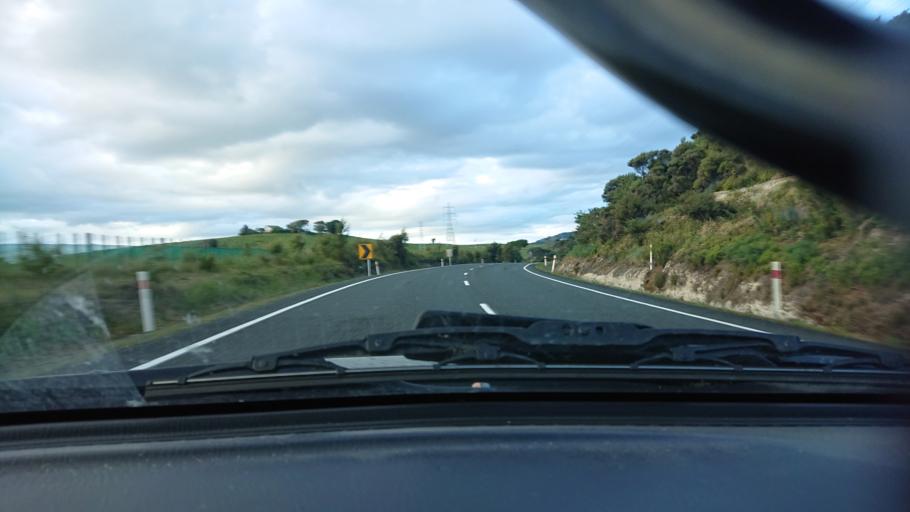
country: NZ
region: Auckland
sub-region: Auckland
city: Parakai
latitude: -36.4797
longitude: 174.4475
